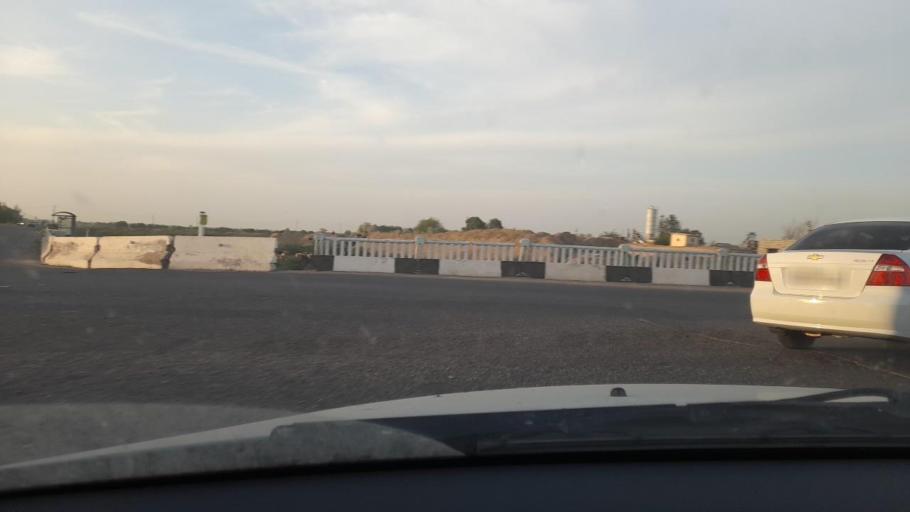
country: UZ
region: Sirdaryo
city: Guliston
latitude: 40.5084
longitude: 68.7318
